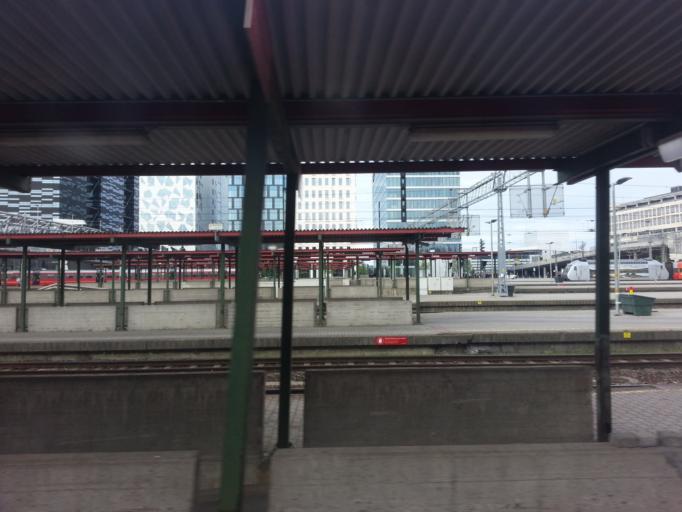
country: NO
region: Oslo
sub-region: Oslo
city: Oslo
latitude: 59.9103
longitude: 10.7588
